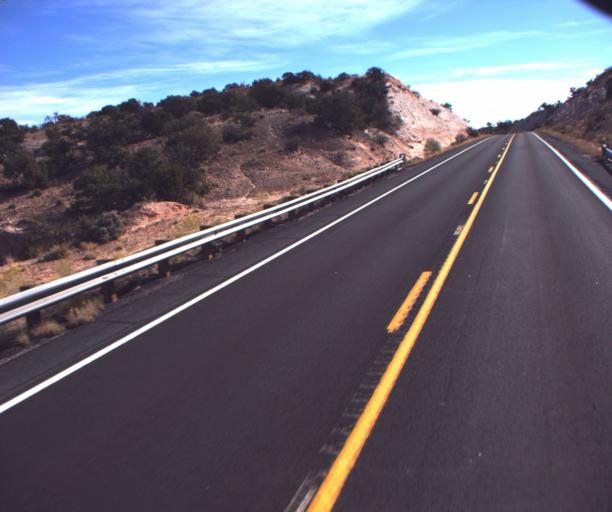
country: US
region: Arizona
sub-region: Coconino County
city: Kaibito
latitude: 36.5922
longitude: -110.8974
